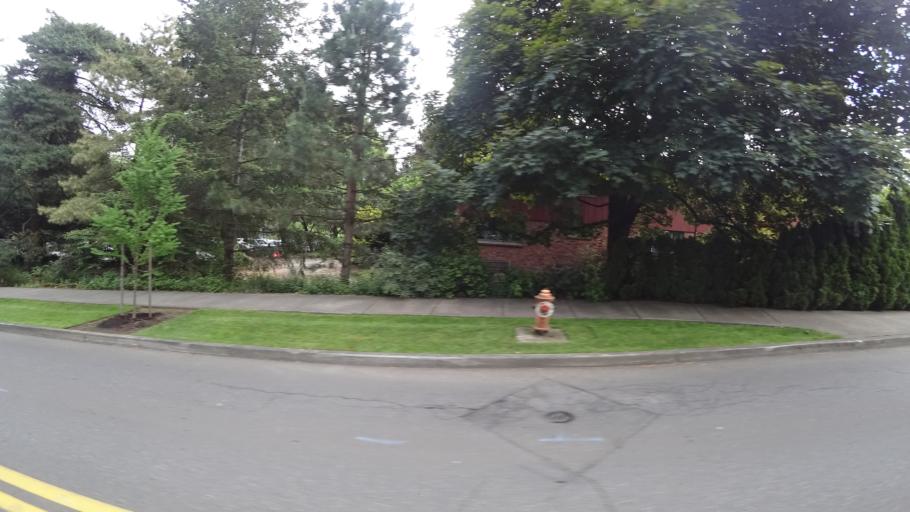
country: US
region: Oregon
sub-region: Clackamas County
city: Lake Oswego
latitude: 45.4495
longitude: -122.6727
